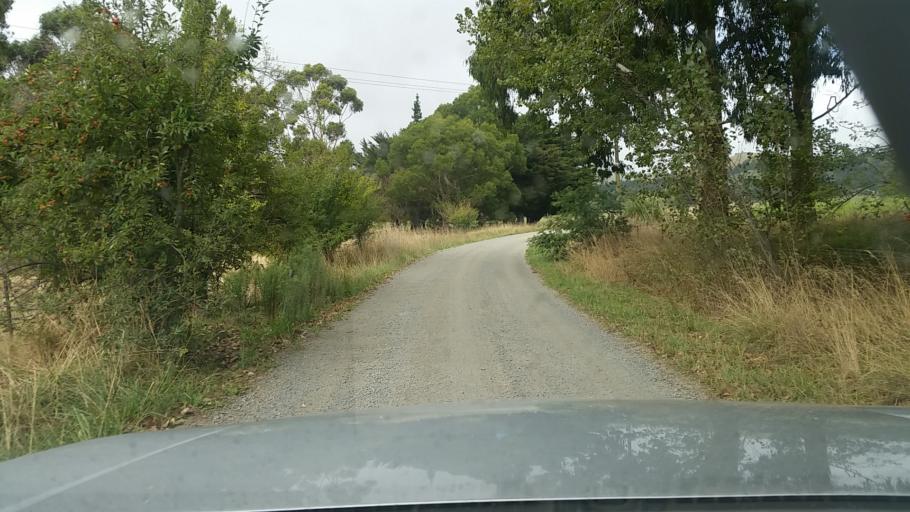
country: NZ
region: Marlborough
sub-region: Marlborough District
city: Blenheim
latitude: -41.7248
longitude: 173.9252
